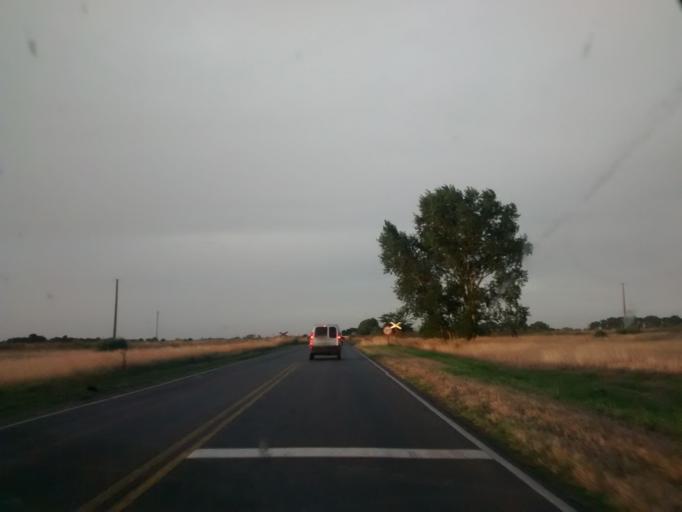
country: AR
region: Buenos Aires
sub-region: Partido de General Belgrano
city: General Belgrano
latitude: -35.8873
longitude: -58.6184
